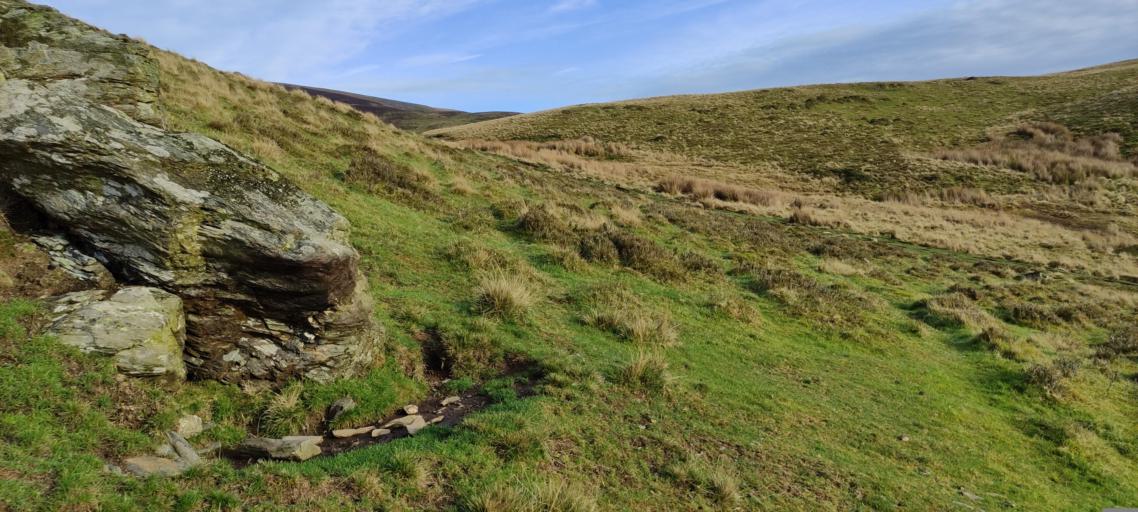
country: GB
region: England
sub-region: Cumbria
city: Millom
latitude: 54.2417
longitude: -3.3361
